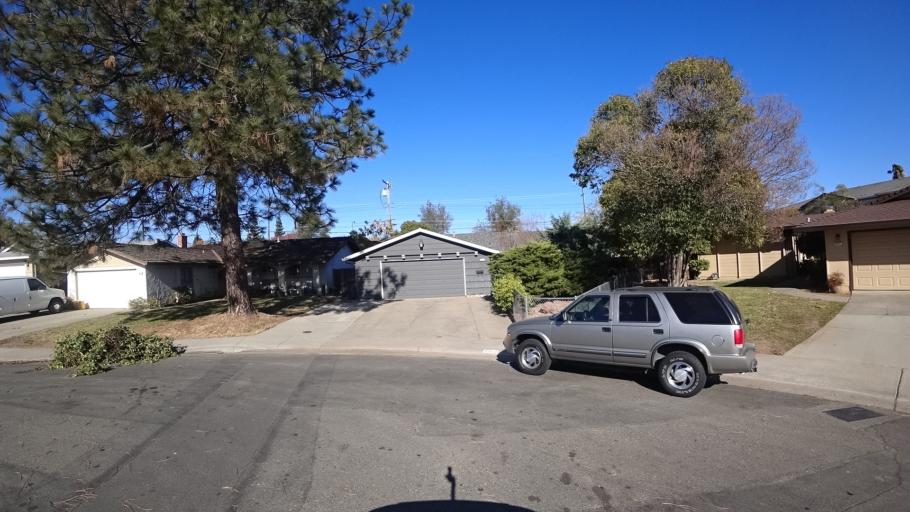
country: US
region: California
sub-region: Sacramento County
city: Antelope
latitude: 38.6772
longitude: -121.3131
